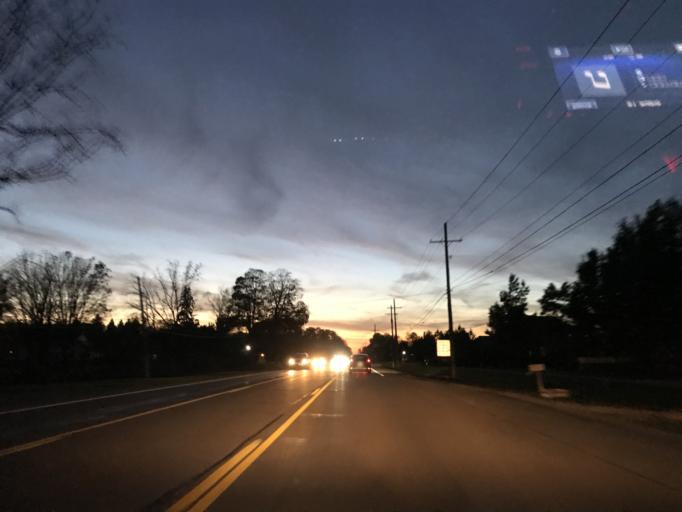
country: US
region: Michigan
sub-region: Wayne County
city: Northville
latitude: 42.4362
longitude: -83.5214
